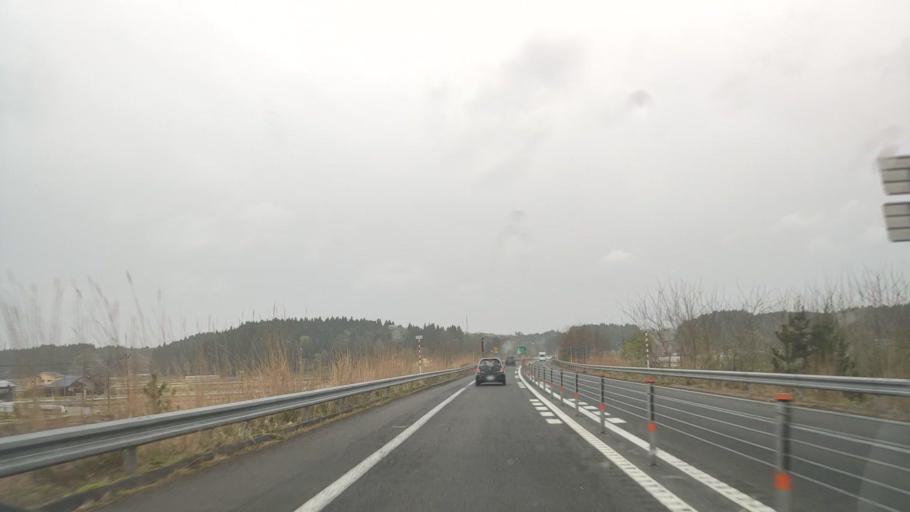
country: JP
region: Akita
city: Noshiromachi
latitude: 40.1872
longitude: 140.0992
